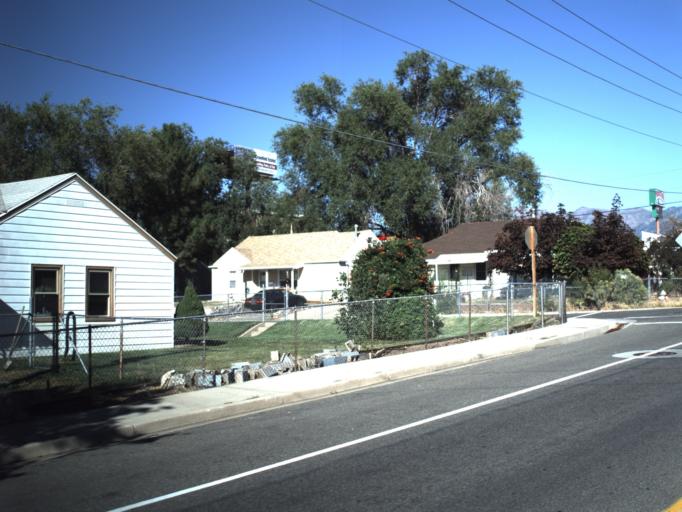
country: US
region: Utah
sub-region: Davis County
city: Sunset
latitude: 41.1399
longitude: -112.0279
